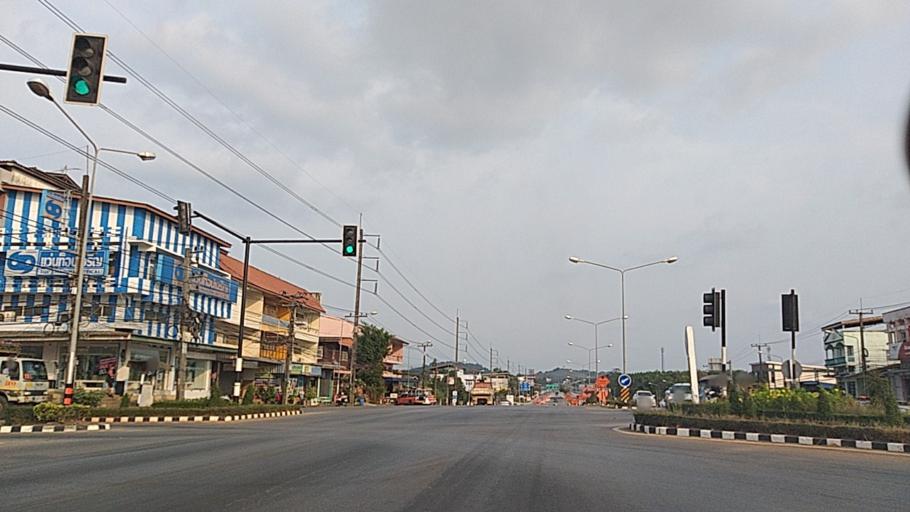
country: TH
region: Trat
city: Khao Saming
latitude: 12.3759
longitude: 102.3819
